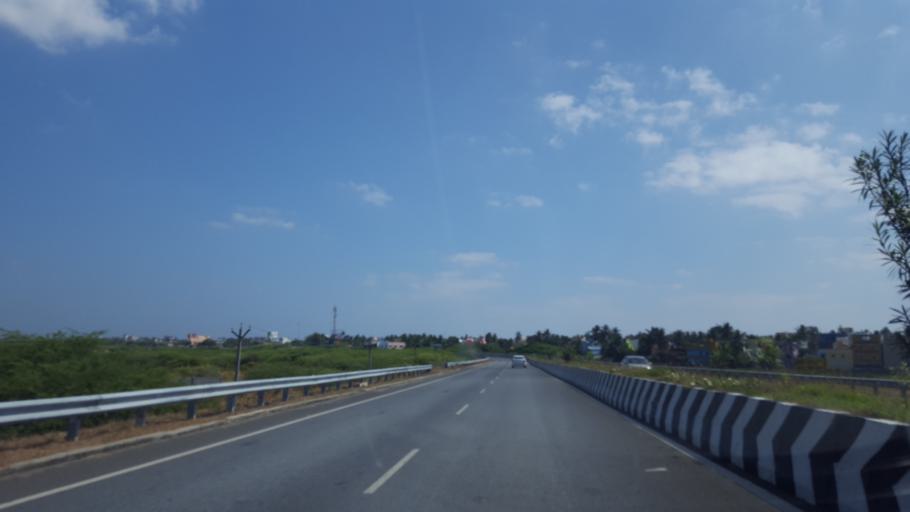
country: IN
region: Tamil Nadu
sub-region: Kancheepuram
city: Mamallapuram
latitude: 12.6229
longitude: 80.1884
